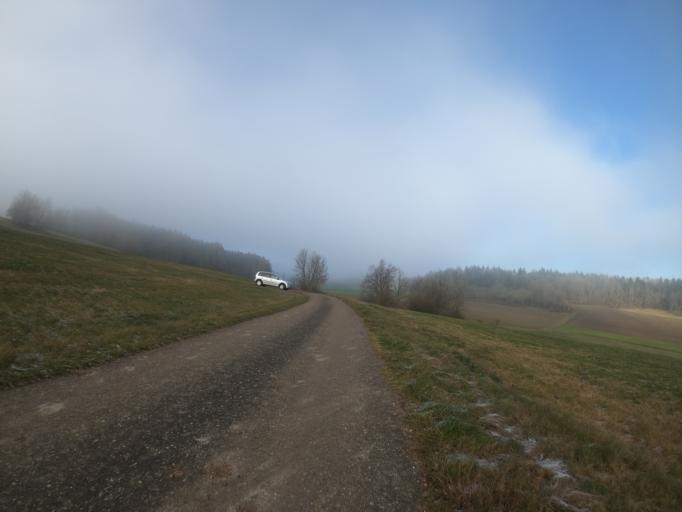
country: DE
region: Baden-Wuerttemberg
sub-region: Regierungsbezirk Stuttgart
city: Deggingen
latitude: 48.5921
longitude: 9.7511
